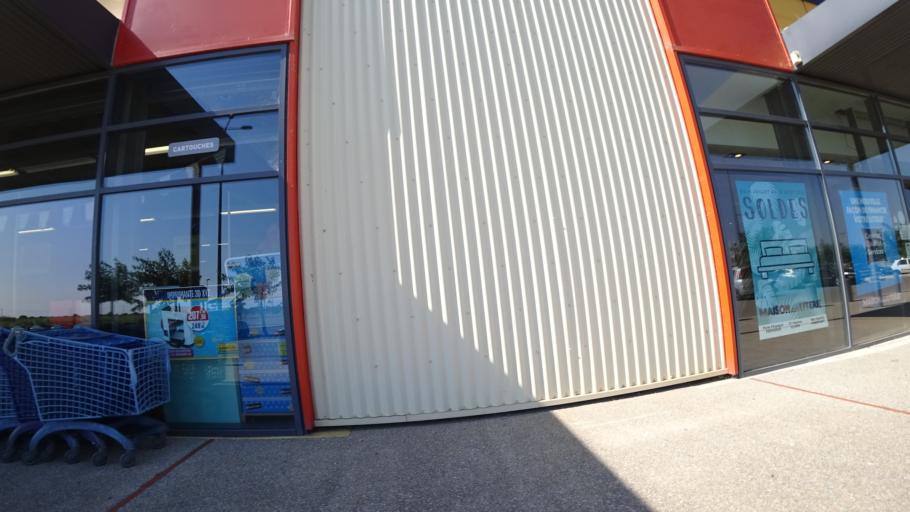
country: FR
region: Languedoc-Roussillon
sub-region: Departement des Pyrenees-Orientales
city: Pia
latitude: 42.7712
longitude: 2.9169
